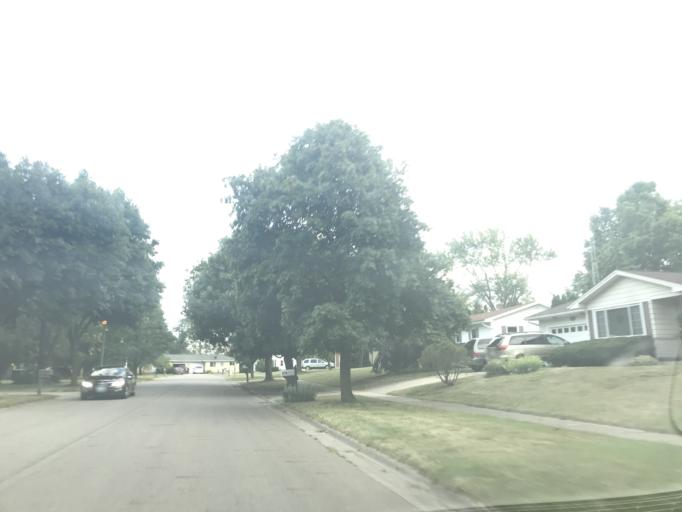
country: US
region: Michigan
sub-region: Eaton County
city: Waverly
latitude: 42.7229
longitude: -84.6094
